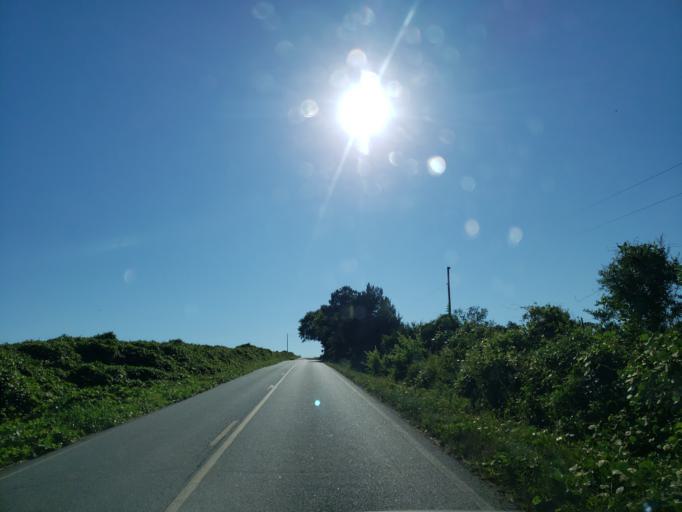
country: US
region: Georgia
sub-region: Bartow County
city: Euharlee
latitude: 34.1043
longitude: -84.9835
